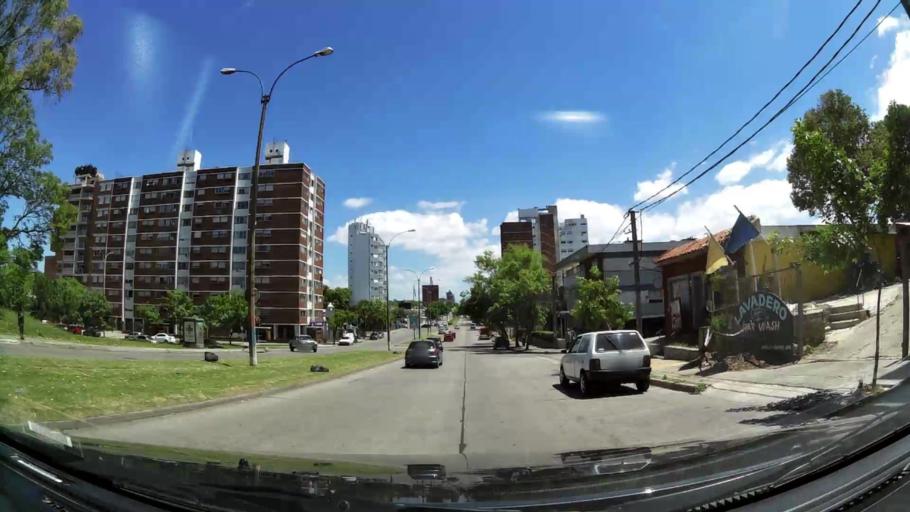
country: UY
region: Montevideo
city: Montevideo
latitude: -34.8939
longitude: -56.1286
